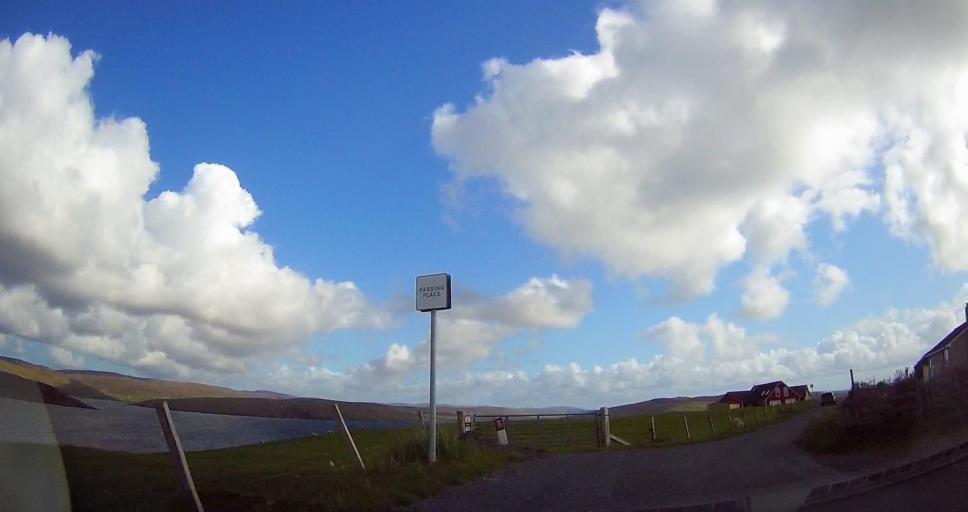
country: GB
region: Scotland
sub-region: Shetland Islands
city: Lerwick
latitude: 60.3607
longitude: -1.3834
